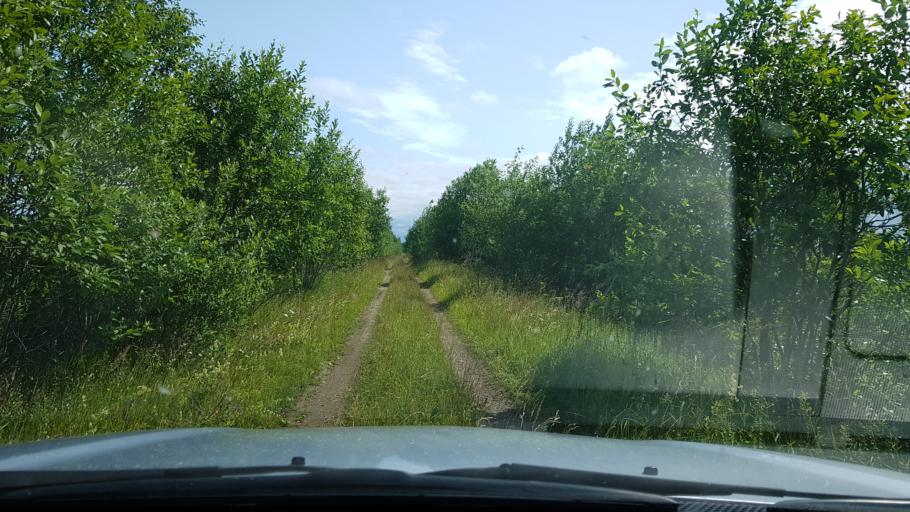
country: EE
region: Ida-Virumaa
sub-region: Sillamaee linn
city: Sillamae
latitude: 59.3668
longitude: 27.7919
